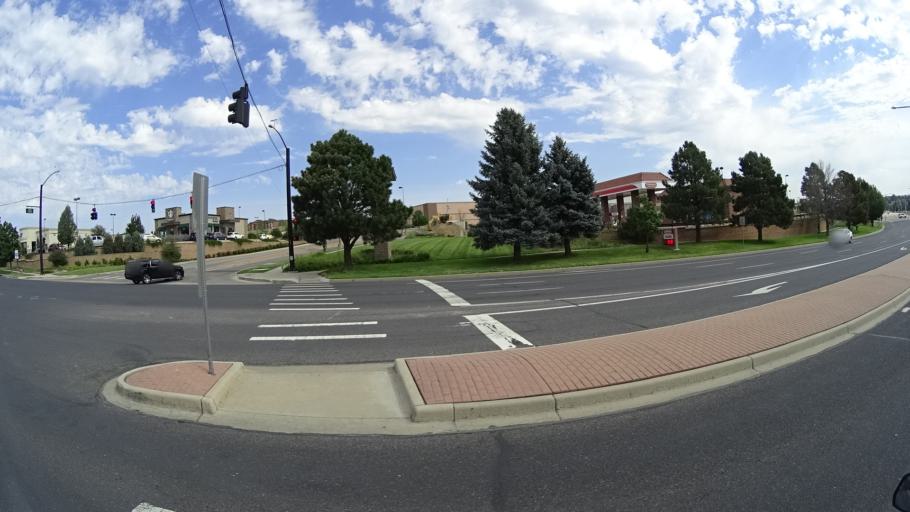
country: US
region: Colorado
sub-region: El Paso County
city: Cimarron Hills
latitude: 38.8935
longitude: -104.7168
